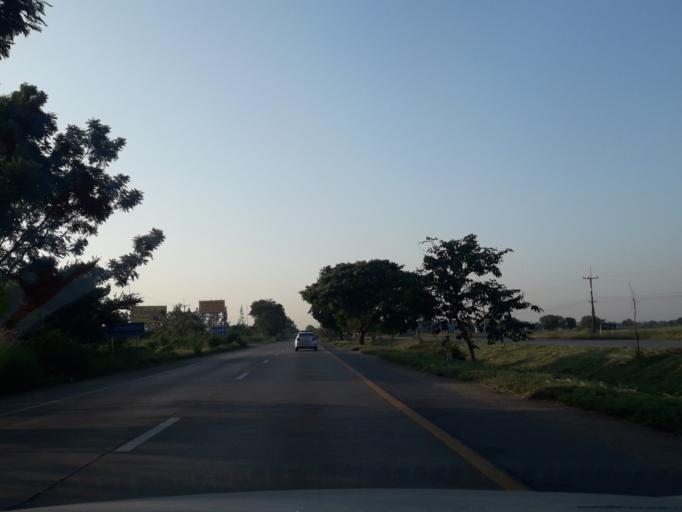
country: TH
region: Phra Nakhon Si Ayutthaya
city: Bang Pa-in
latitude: 14.2588
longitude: 100.5345
